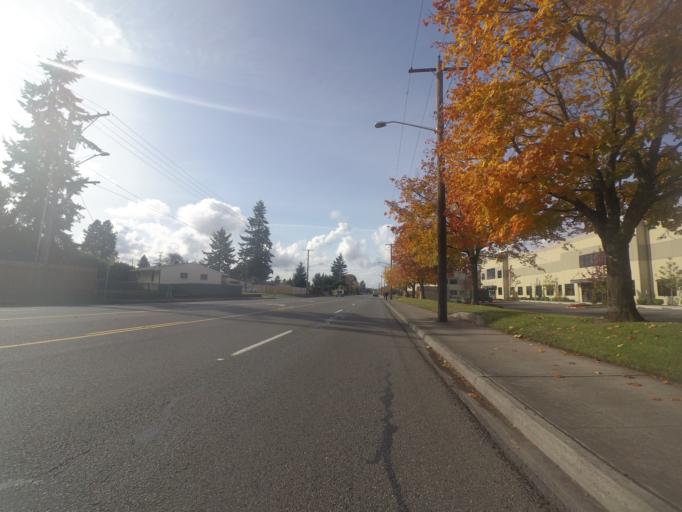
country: US
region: Washington
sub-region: Pierce County
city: Lakewood
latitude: 47.1667
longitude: -122.4987
